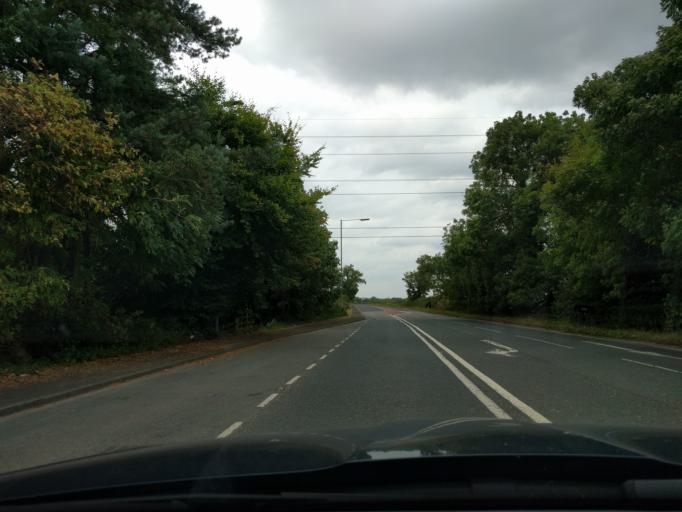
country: GB
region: England
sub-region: Northumberland
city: Stannington
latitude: 55.1364
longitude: -1.6491
